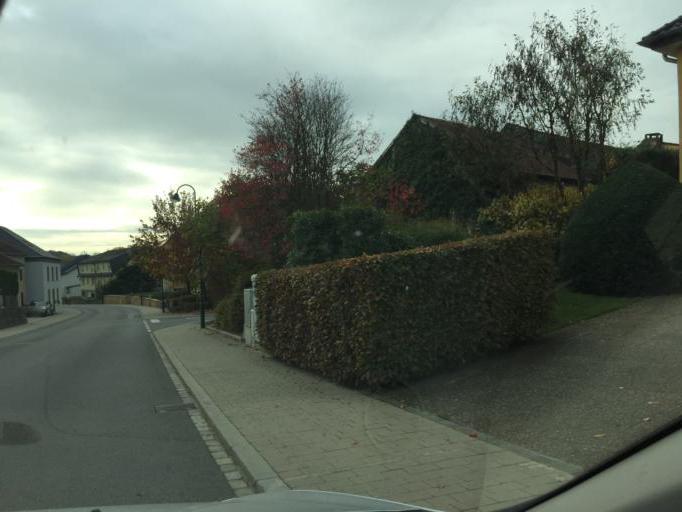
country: LU
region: Luxembourg
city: Capellen
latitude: 49.6172
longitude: 5.9862
